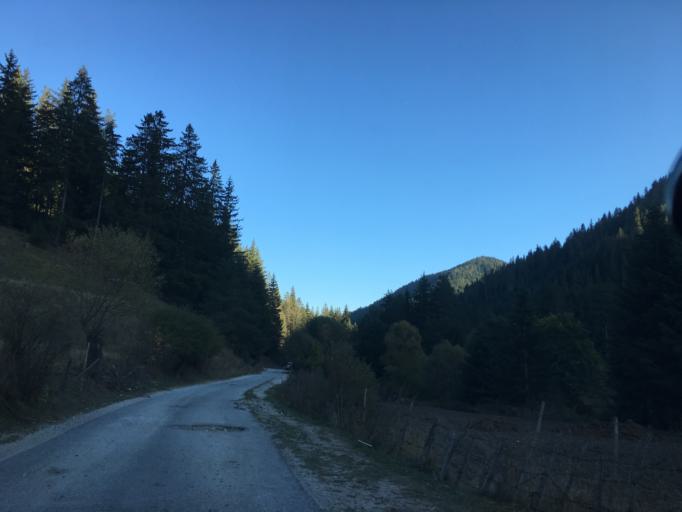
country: BG
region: Smolyan
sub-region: Obshtina Borino
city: Borino
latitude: 41.5893
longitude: 24.3846
